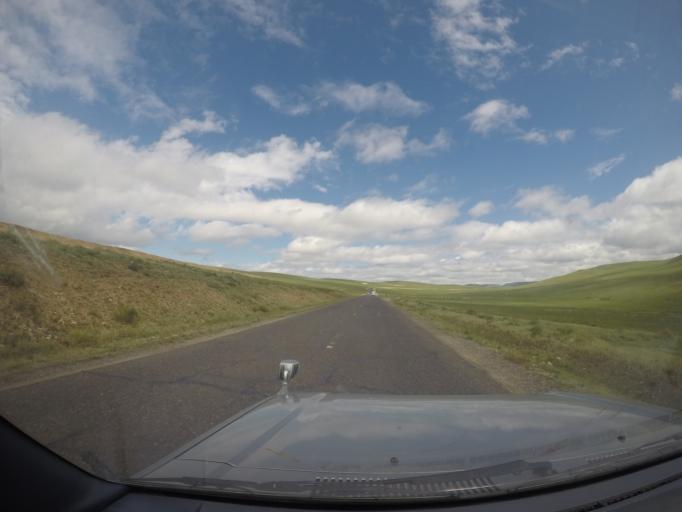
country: MN
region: Hentiy
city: Modot
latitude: 47.8055
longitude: 108.7233
